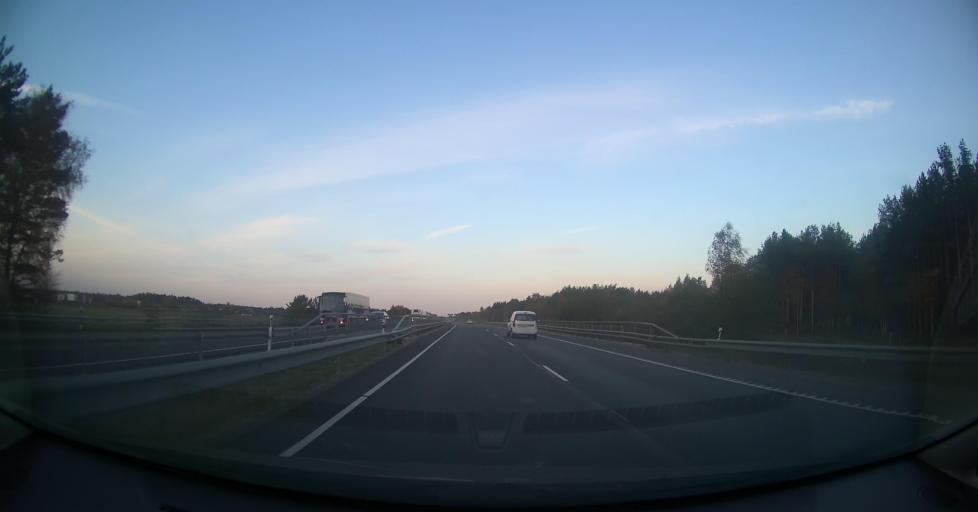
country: EE
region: Harju
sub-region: Saku vald
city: Saku
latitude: 59.3162
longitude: 24.6614
